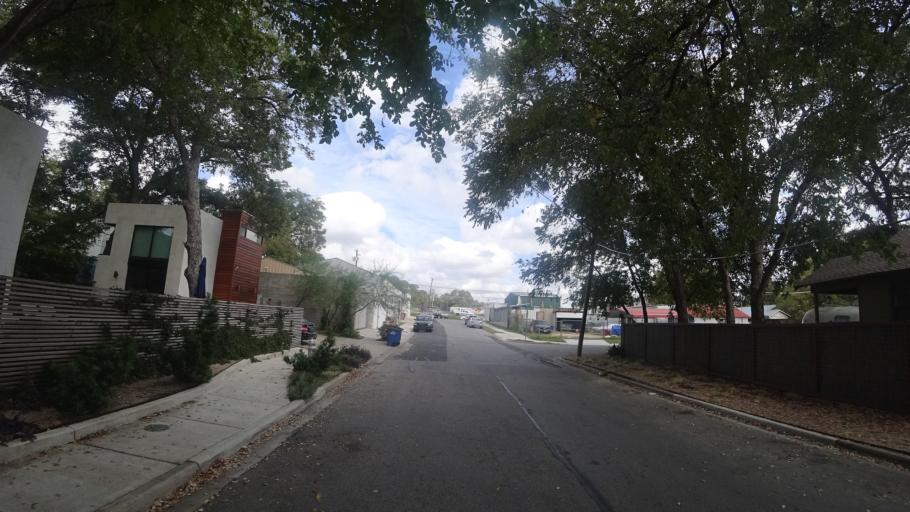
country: US
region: Texas
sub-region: Travis County
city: Austin
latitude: 30.2568
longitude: -97.7141
